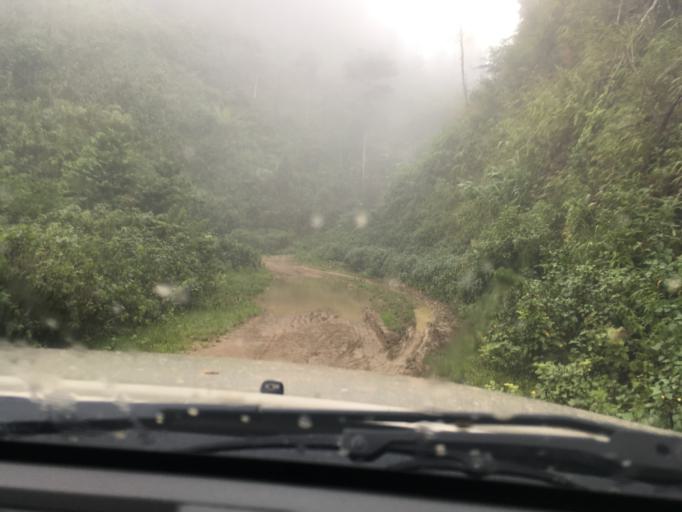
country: LA
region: Phongsali
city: Phongsali
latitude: 21.3984
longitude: 102.1901
